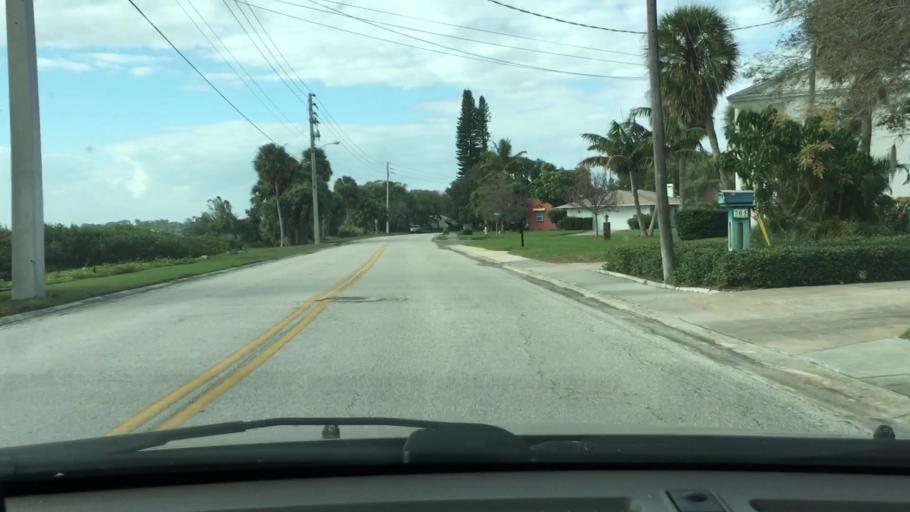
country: US
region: Florida
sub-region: Brevard County
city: Melbourne Beach
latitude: 28.0710
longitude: -80.5669
